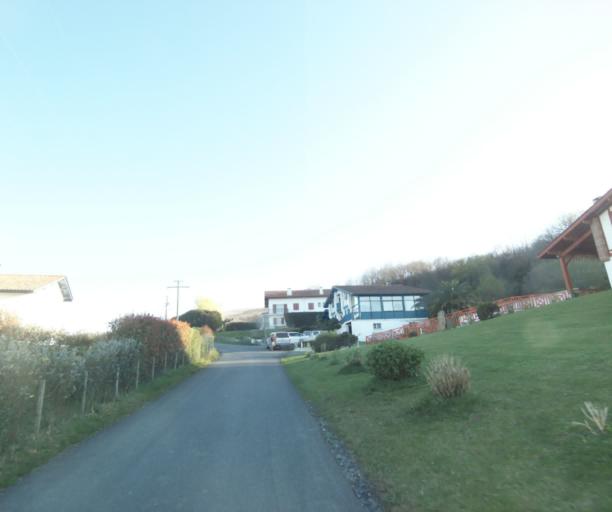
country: FR
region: Aquitaine
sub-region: Departement des Pyrenees-Atlantiques
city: Urrugne
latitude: 43.3506
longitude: -1.7220
